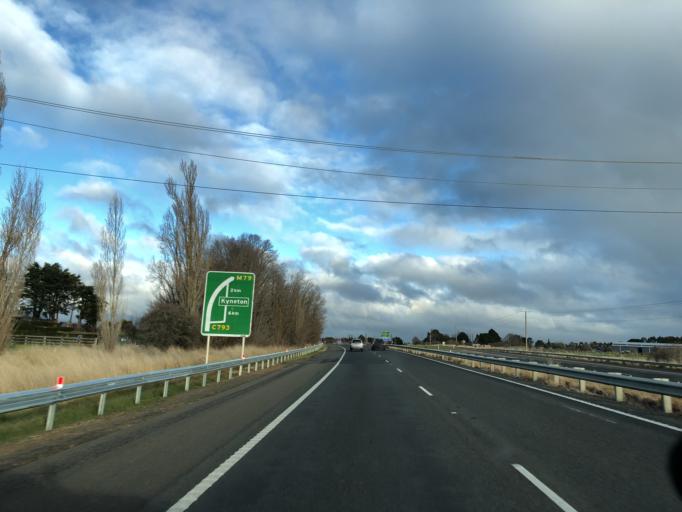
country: AU
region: Victoria
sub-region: Mount Alexander
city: Castlemaine
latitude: -37.2163
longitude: 144.4147
